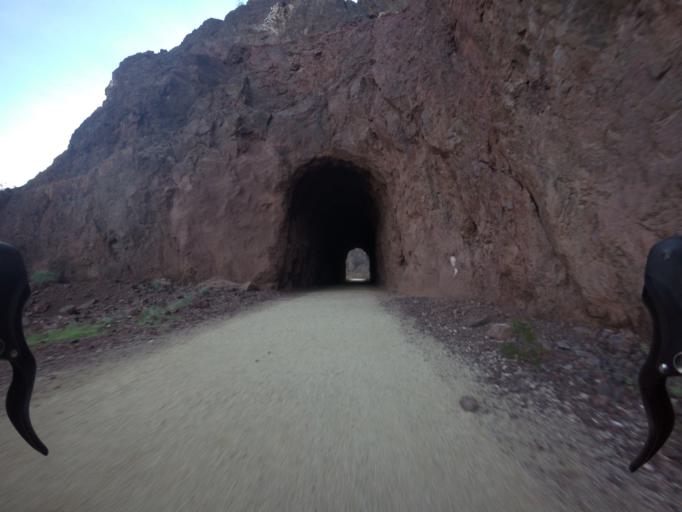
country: US
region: Nevada
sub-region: Clark County
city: Boulder City
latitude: 36.0163
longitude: -114.7664
